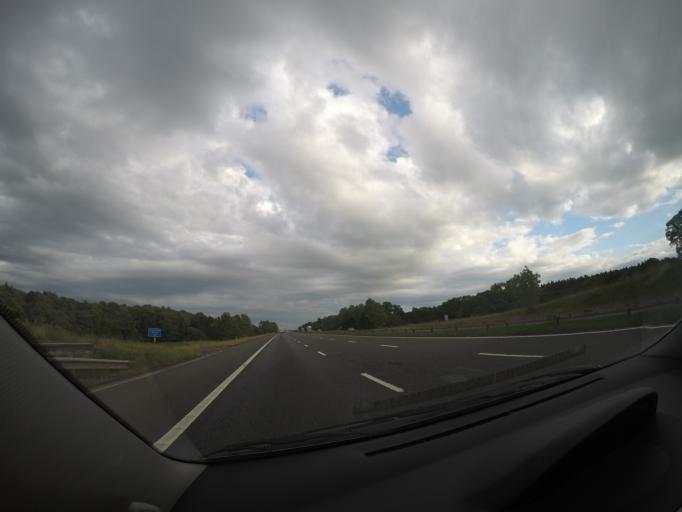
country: GB
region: England
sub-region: Cumbria
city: Penrith
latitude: 54.7457
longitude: -2.8121
